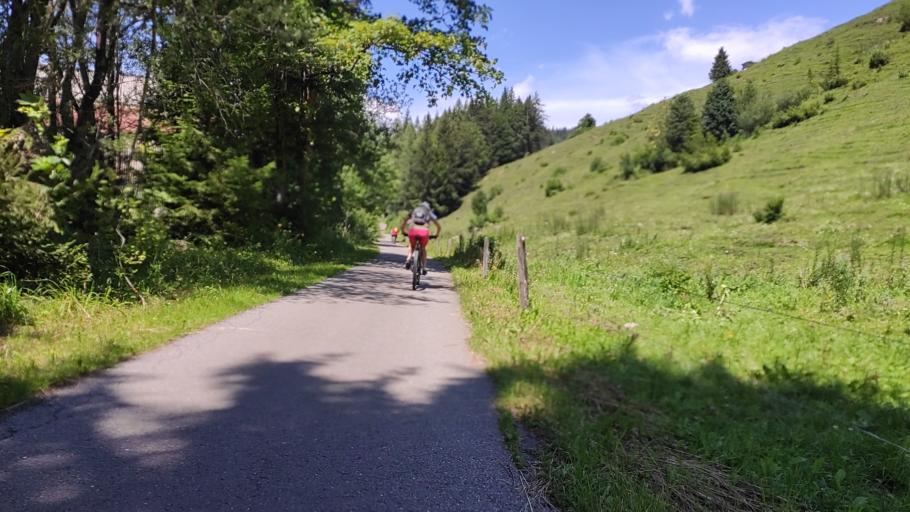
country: AT
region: Tyrol
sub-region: Politischer Bezirk Kitzbuhel
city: Hochfilzen
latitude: 47.4670
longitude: 12.6359
